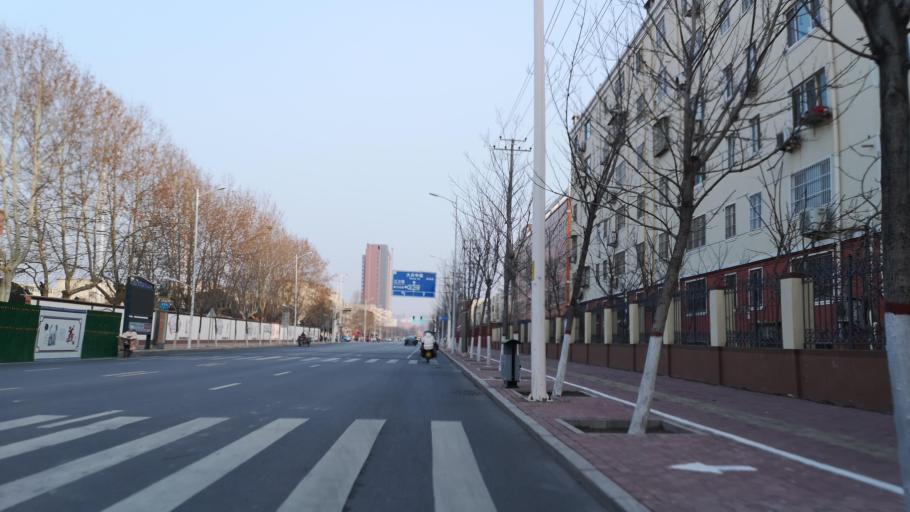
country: CN
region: Henan Sheng
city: Zhongyuanlu
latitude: 35.7635
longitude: 115.0605
